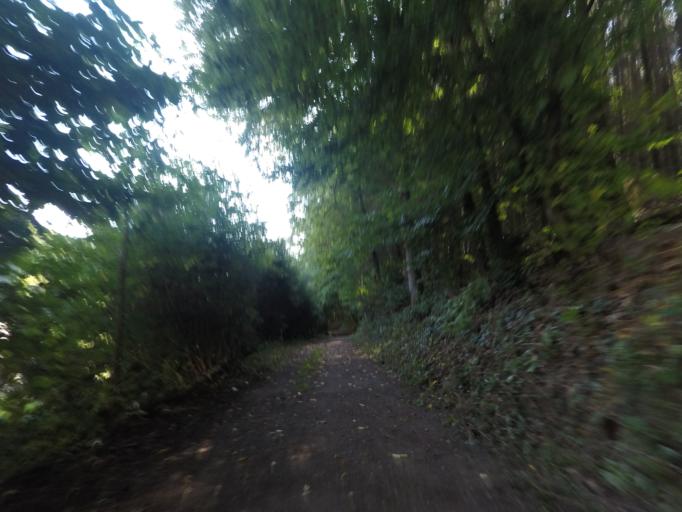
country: LU
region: Luxembourg
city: Bereldange
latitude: 49.6351
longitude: 6.1152
